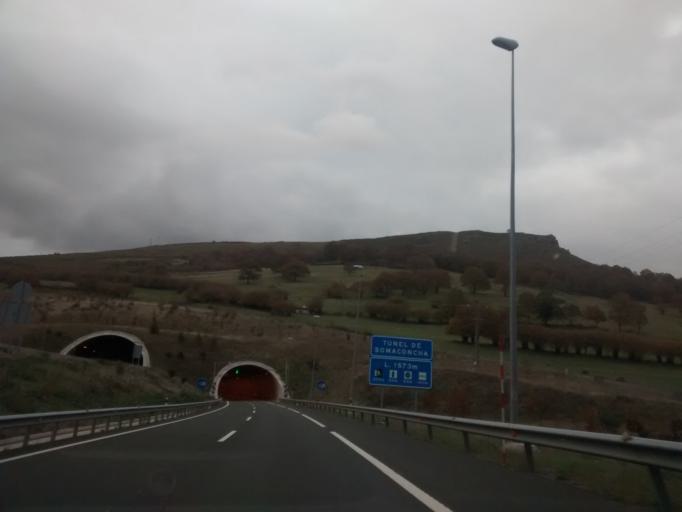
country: ES
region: Cantabria
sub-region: Provincia de Cantabria
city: Pesquera
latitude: 43.0875
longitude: -4.0800
